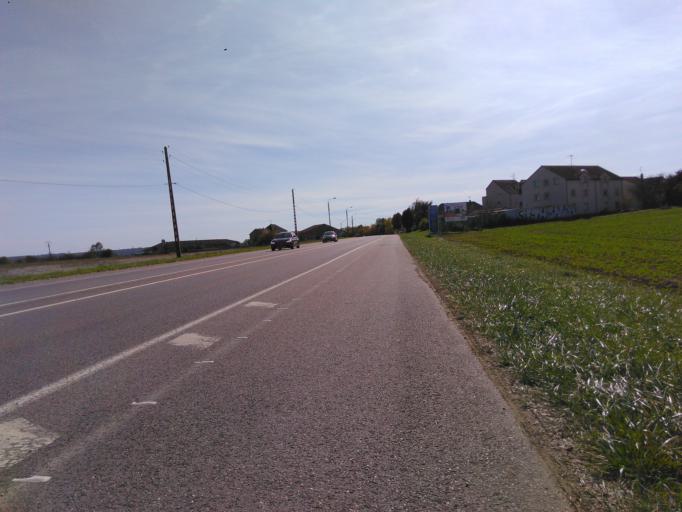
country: FR
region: Lorraine
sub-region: Departement de la Moselle
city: Thionville
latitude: 49.3871
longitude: 6.1685
